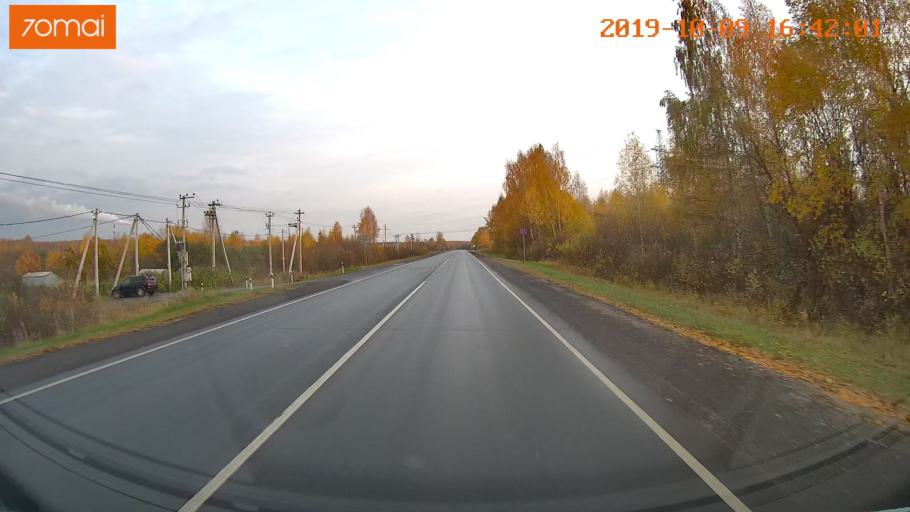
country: RU
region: Kostroma
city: Volgorechensk
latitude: 57.4668
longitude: 41.0921
